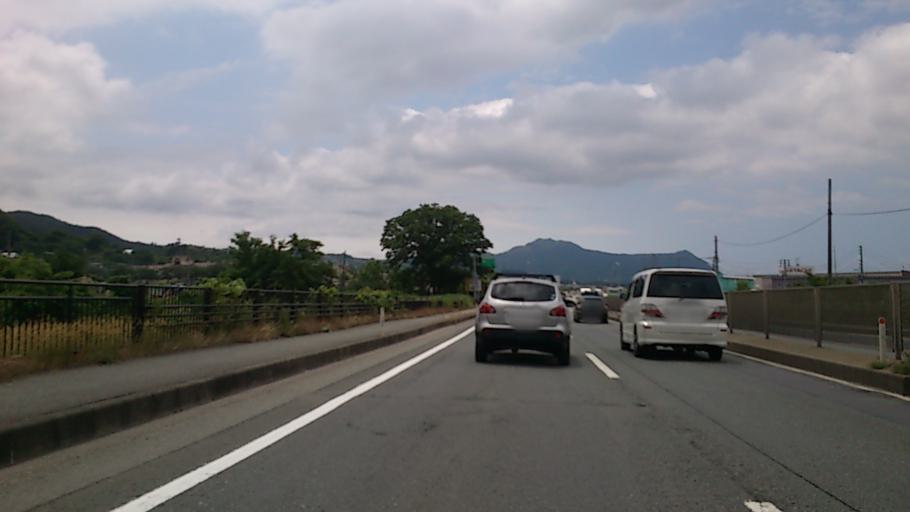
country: JP
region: Yamagata
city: Kaminoyama
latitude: 38.2011
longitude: 140.3147
